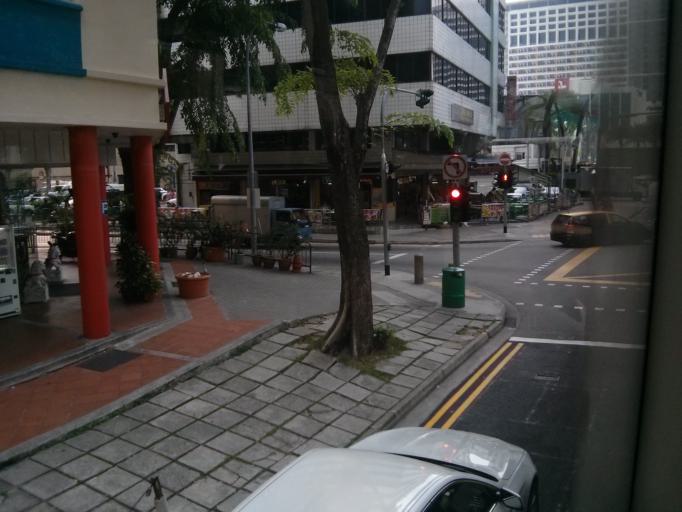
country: SG
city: Singapore
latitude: 1.3103
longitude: 103.8568
